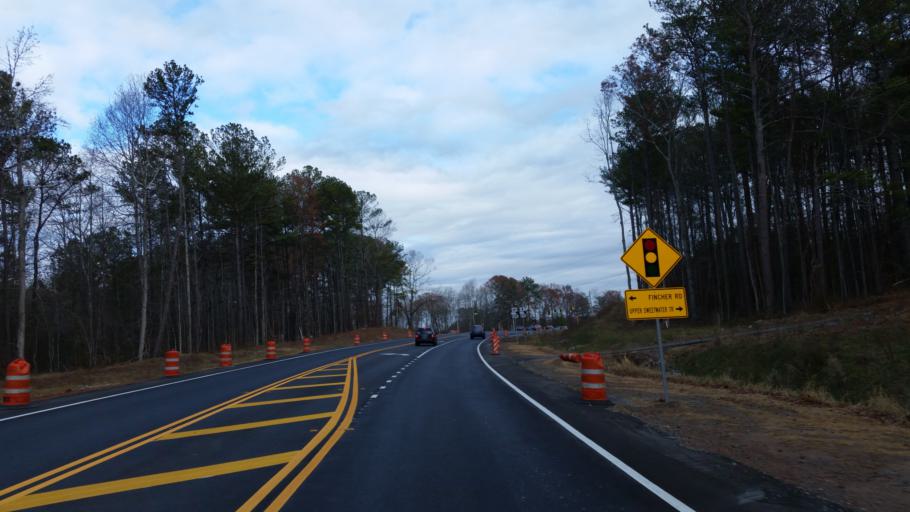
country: US
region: Georgia
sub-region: Cherokee County
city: Holly Springs
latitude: 34.2227
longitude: -84.6207
